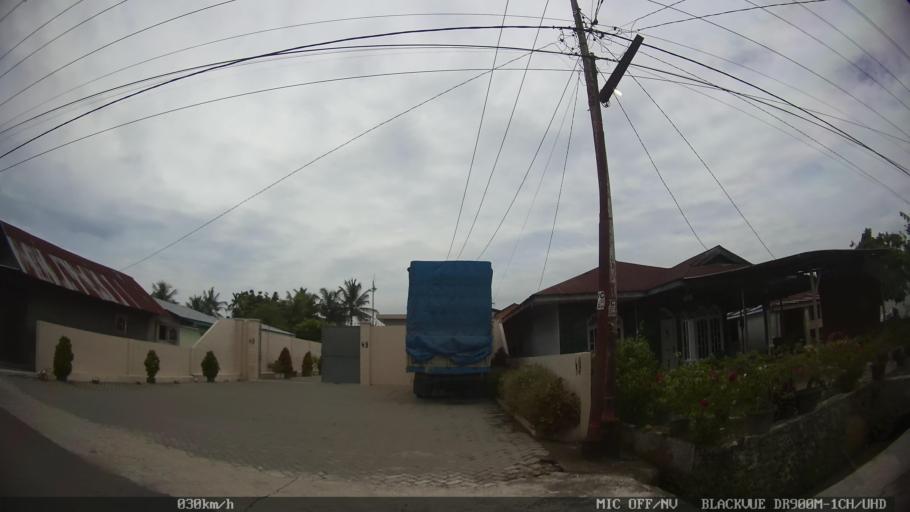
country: ID
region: North Sumatra
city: Sunggal
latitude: 3.6298
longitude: 98.5589
